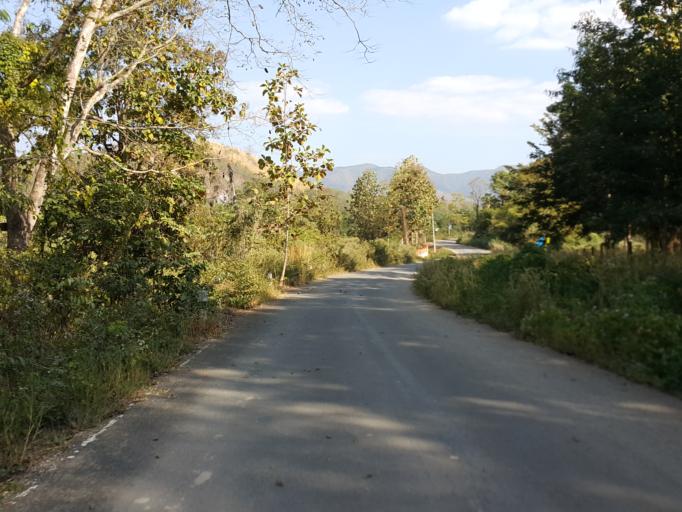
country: TH
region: Chiang Mai
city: Mae On
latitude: 18.7933
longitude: 99.2340
